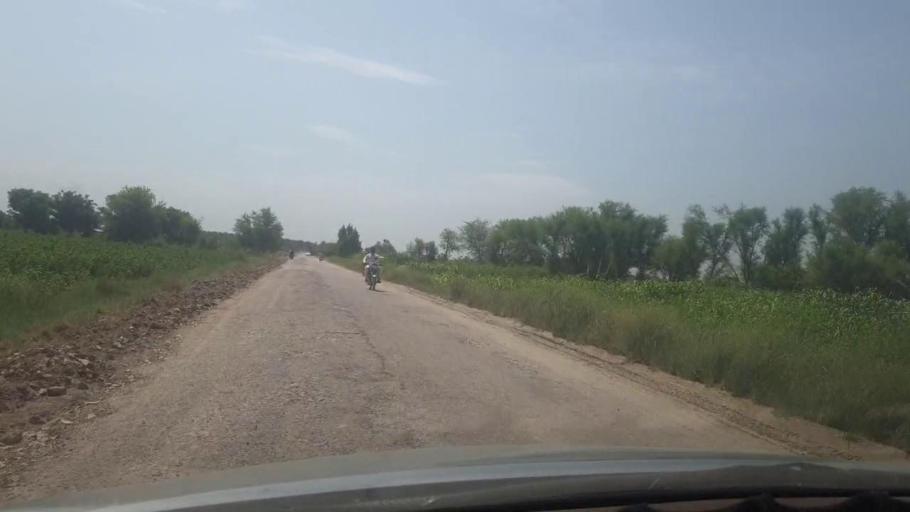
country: PK
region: Sindh
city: Bozdar
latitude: 27.2135
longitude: 68.5736
